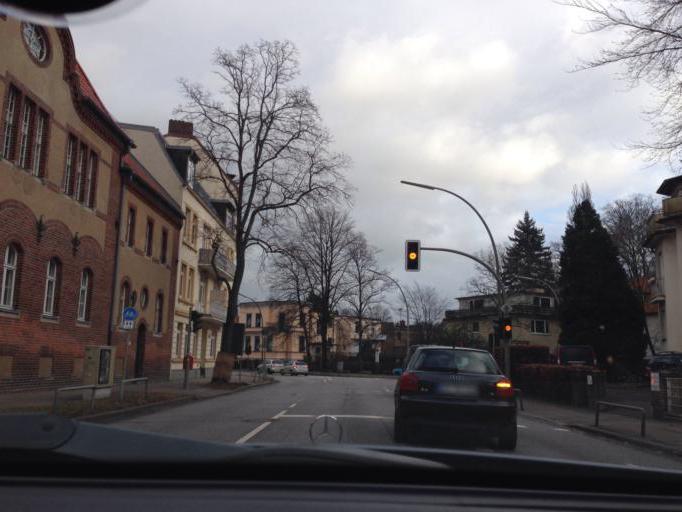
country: DE
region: Hamburg
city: Marienthal
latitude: 53.5723
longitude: 10.0750
